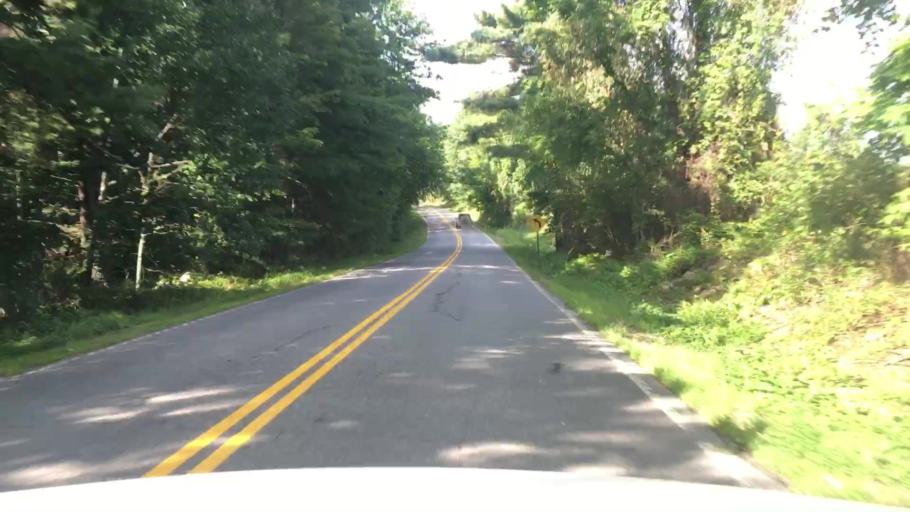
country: US
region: New Hampshire
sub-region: Belknap County
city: Gilford
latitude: 43.5606
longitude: -71.4140
